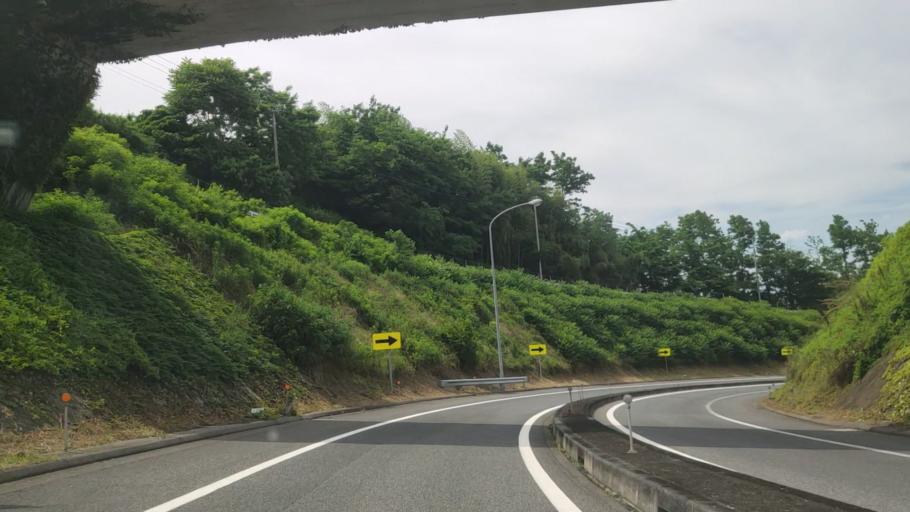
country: JP
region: Gunma
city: Tomioka
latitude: 36.2417
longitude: 138.8906
